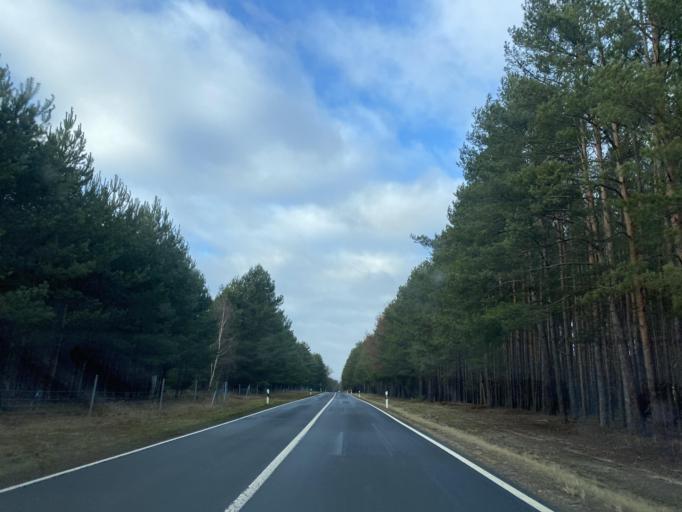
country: PL
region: Lubusz
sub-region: Powiat zarski
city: Leknica
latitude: 51.4982
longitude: 14.8198
